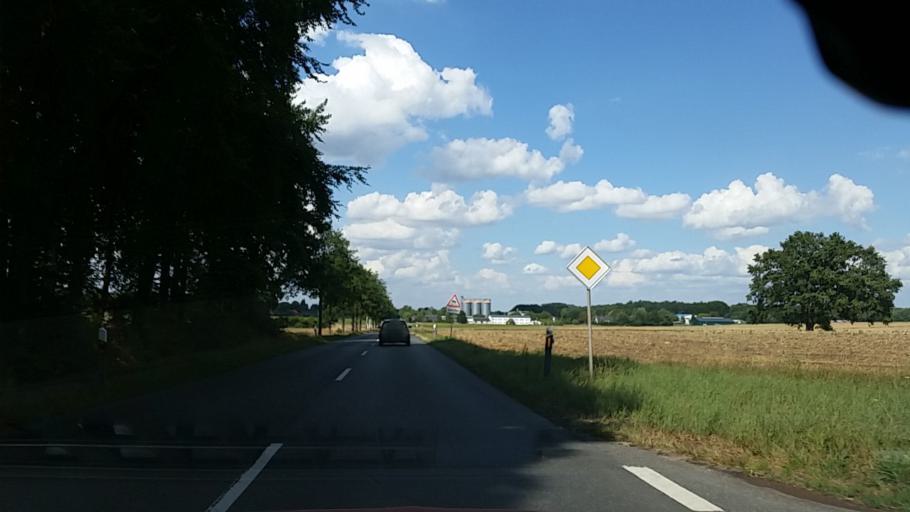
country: DE
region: Lower Saxony
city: Scharnebeck
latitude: 53.2787
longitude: 10.5029
